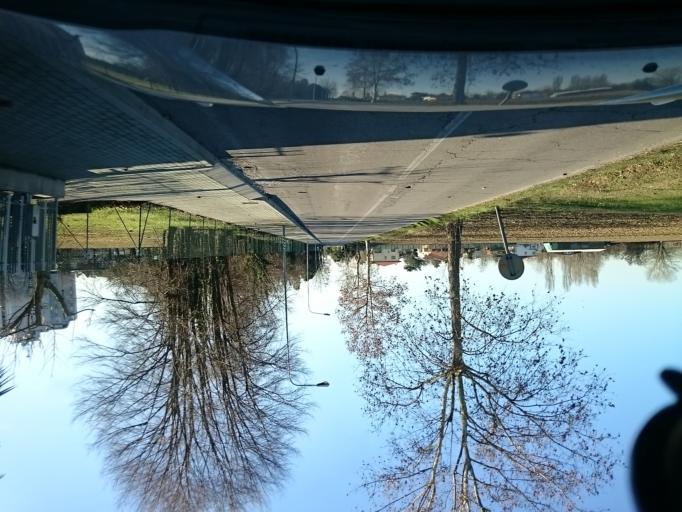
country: IT
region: Veneto
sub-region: Provincia di Padova
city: Montegrotto Terme
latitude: 45.3373
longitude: 11.7916
